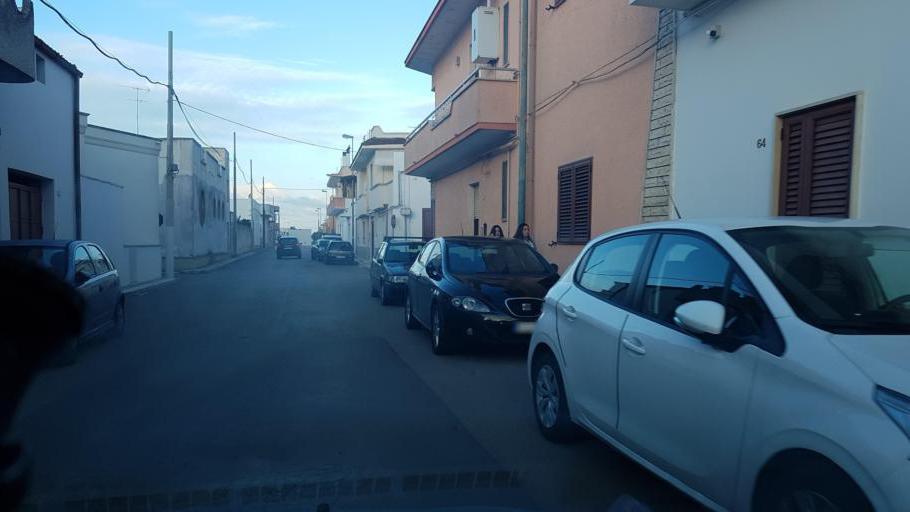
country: IT
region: Apulia
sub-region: Provincia di Brindisi
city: Cellino San Marco
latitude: 40.4684
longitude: 17.9678
